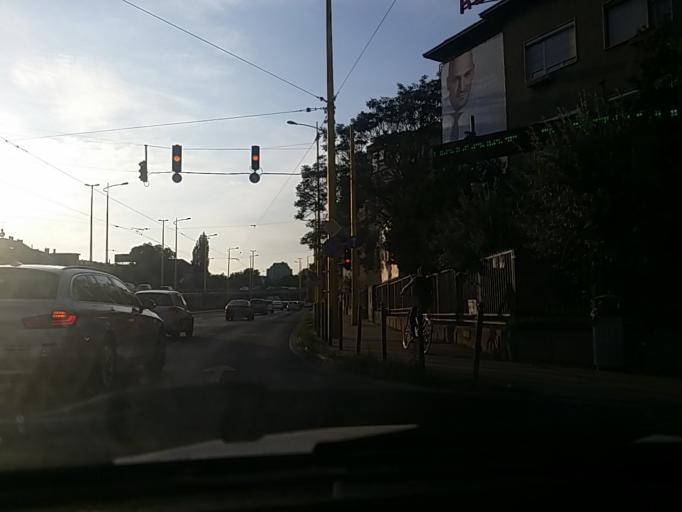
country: HU
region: Budapest
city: Budapest XI. keruelet
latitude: 47.4845
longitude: 19.0263
